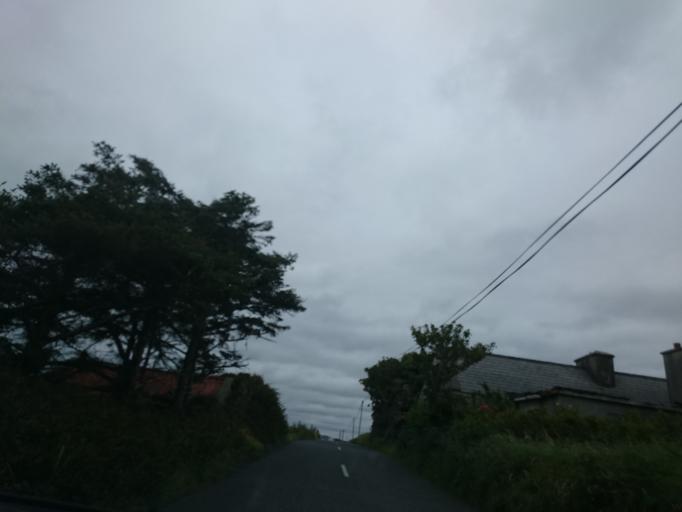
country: IE
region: Connaught
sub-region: County Galway
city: Clifden
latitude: 53.5519
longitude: -10.0987
